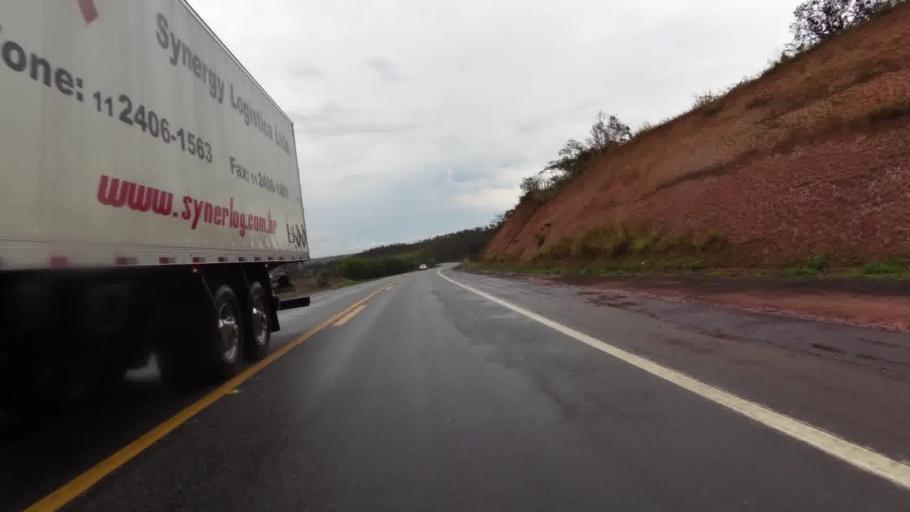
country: BR
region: Rio de Janeiro
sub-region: Campos Dos Goytacazes
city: Campos
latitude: -21.4887
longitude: -41.3410
